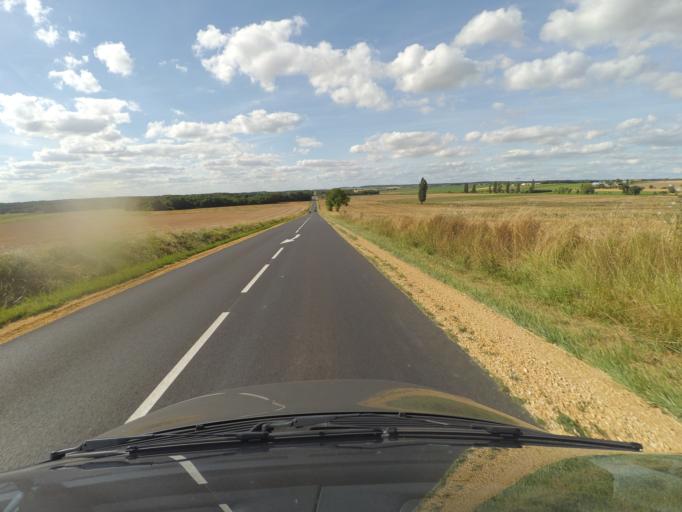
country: FR
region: Poitou-Charentes
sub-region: Departement de la Vienne
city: Saint-Gervais-les-Trois-Clochers
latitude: 46.9246
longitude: 0.4353
